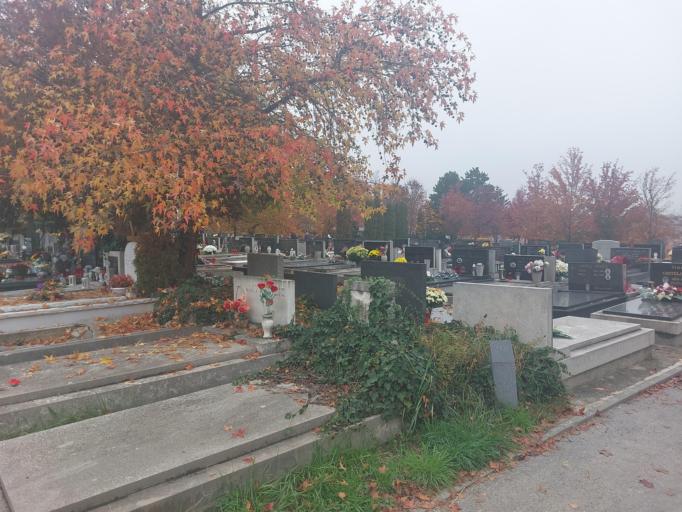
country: HR
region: Grad Zagreb
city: Dubrava
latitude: 45.8434
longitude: 16.0444
